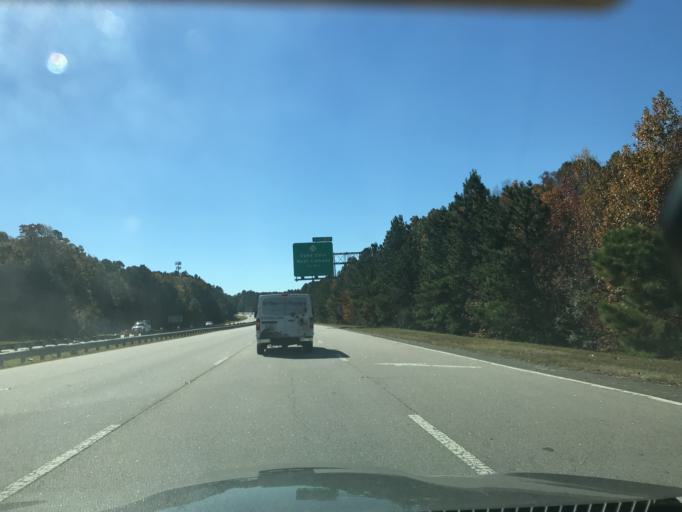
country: US
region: North Carolina
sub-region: Durham County
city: Durham
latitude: 36.0087
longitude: -78.9568
